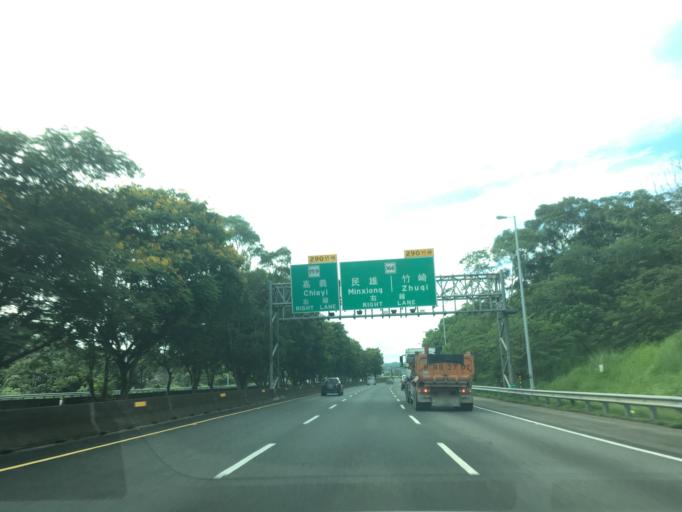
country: TW
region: Taiwan
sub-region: Chiayi
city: Jiayi Shi
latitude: 23.4888
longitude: 120.4956
